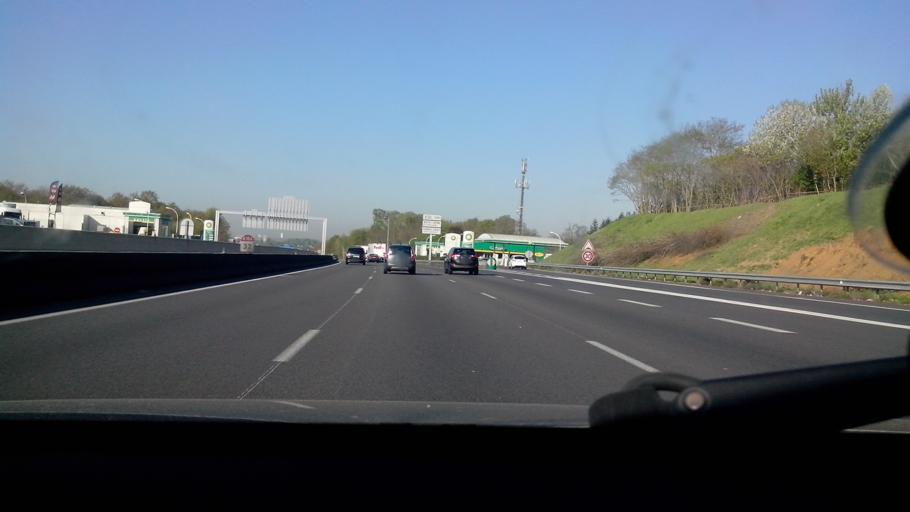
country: FR
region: Ile-de-France
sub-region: Departement de l'Essonne
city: Etiolles
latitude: 48.6311
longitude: 2.4884
